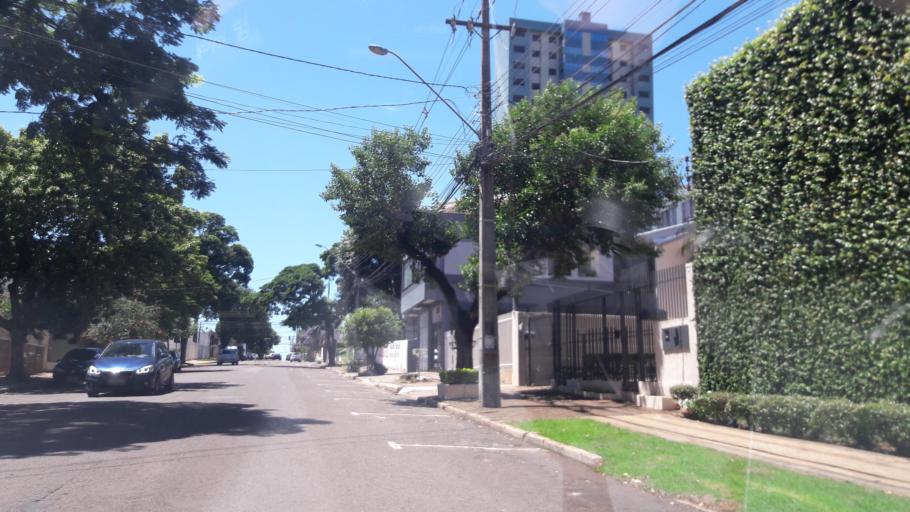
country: BR
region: Parana
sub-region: Cascavel
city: Cascavel
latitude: -24.9501
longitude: -53.4520
